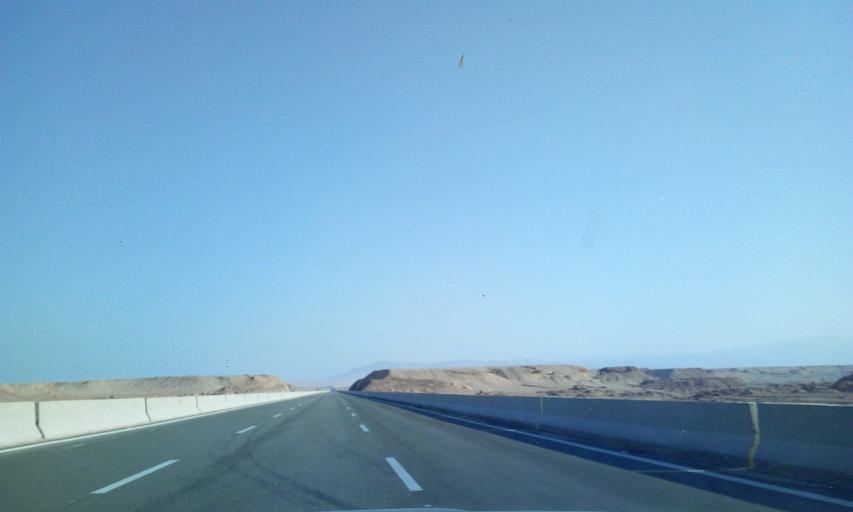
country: EG
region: As Suways
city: Ain Sukhna
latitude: 29.1656
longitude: 32.5091
